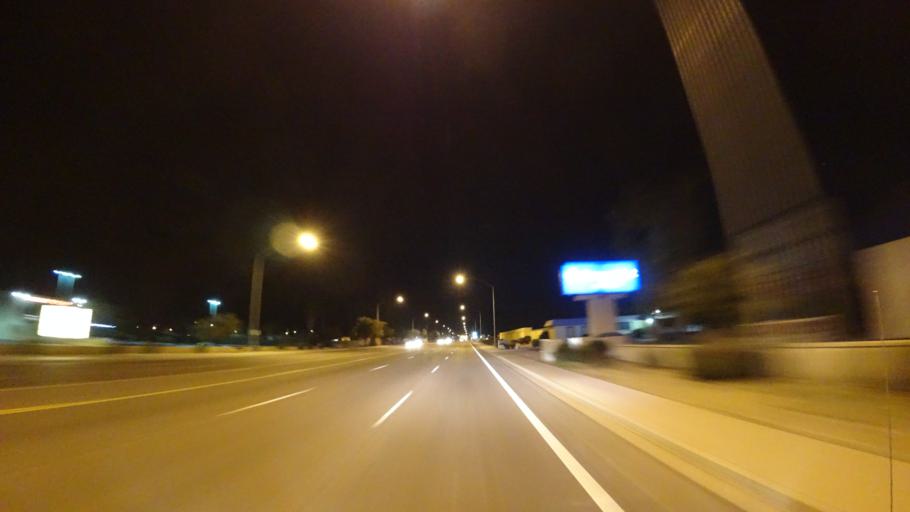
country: US
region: Arizona
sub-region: Maricopa County
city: Mesa
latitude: 33.4514
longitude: -111.8290
